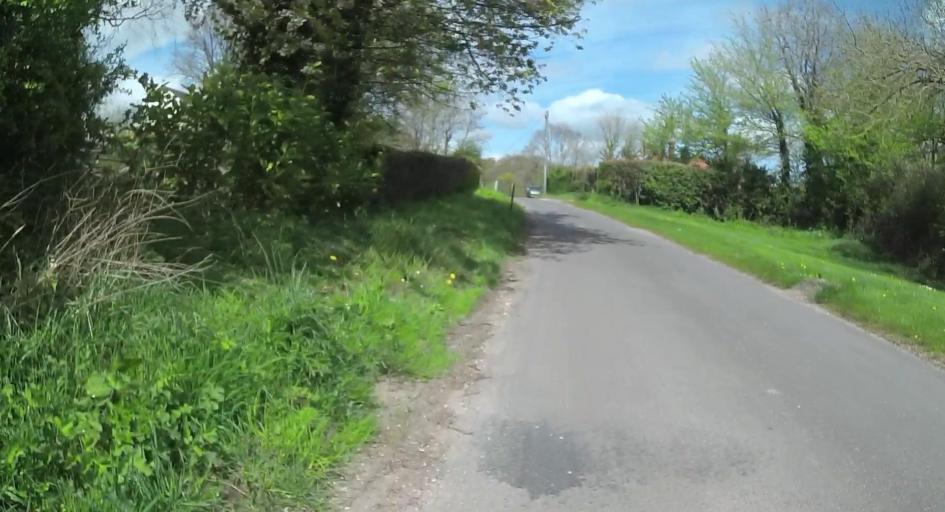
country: GB
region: England
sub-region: Hampshire
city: East Dean
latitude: 51.0633
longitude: -1.5322
